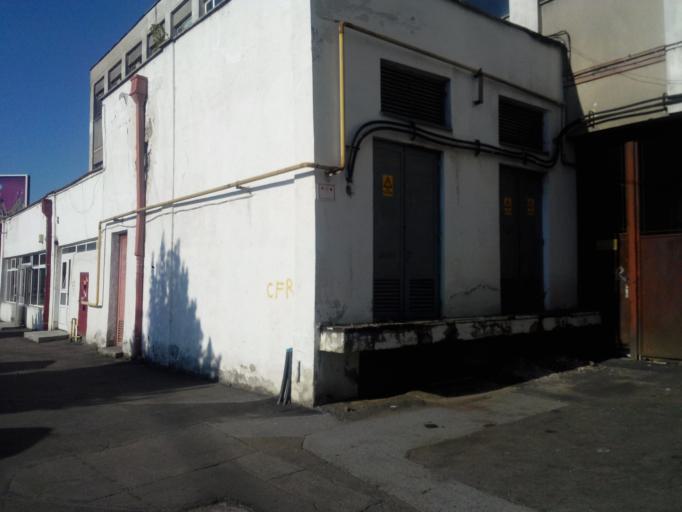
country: RO
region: Cluj
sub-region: Municipiul Cluj-Napoca
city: Cluj-Napoca
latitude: 46.7791
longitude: 23.5917
